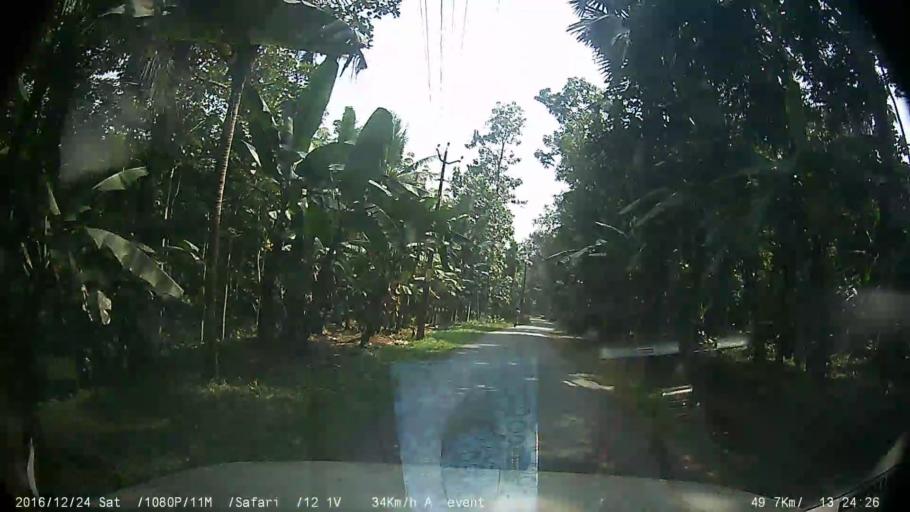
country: IN
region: Kerala
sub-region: Kottayam
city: Palackattumala
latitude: 9.8699
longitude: 76.6773
